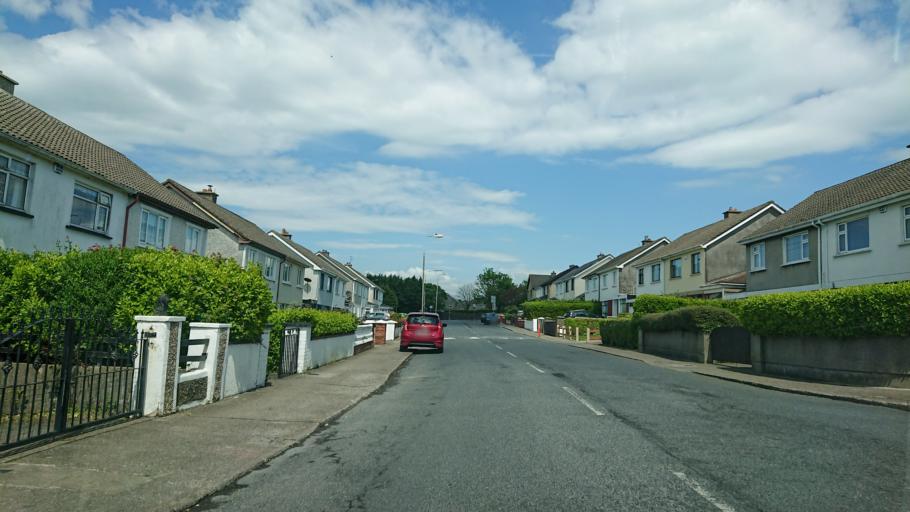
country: IE
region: Munster
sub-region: Waterford
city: Waterford
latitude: 52.2523
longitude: -7.1447
